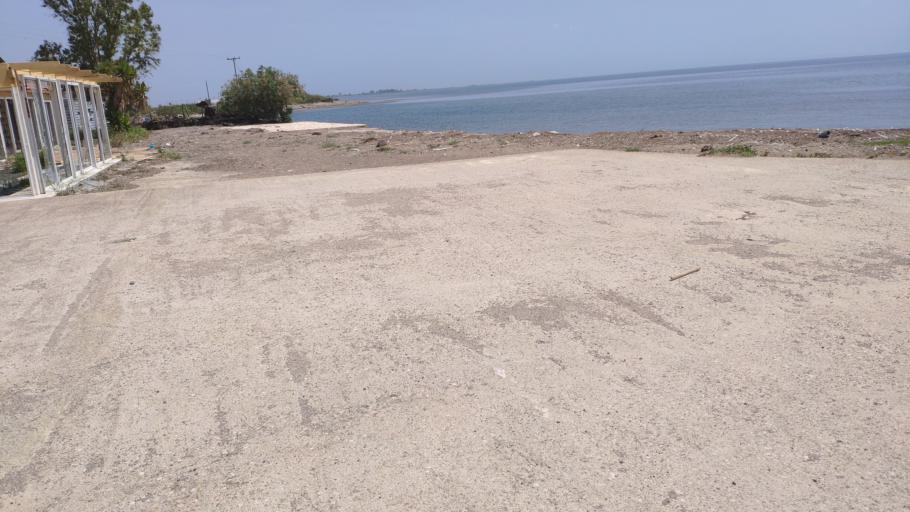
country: GR
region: West Greece
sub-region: Nomos Aitolias kai Akarnanias
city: Mesolongi
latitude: 38.3256
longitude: 21.4215
